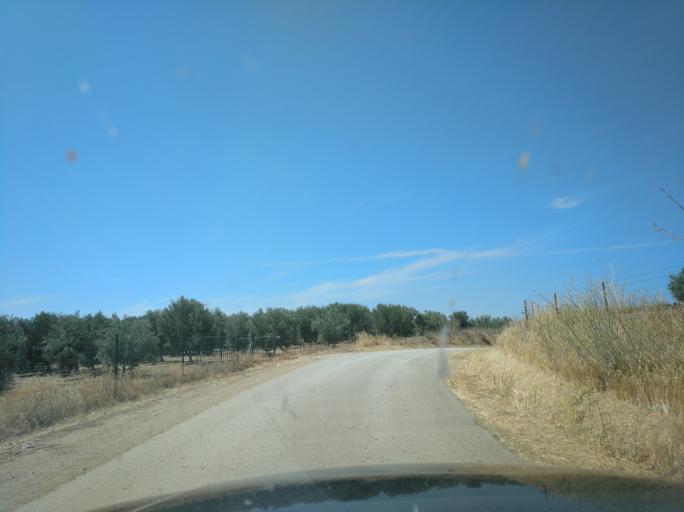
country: PT
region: Portalegre
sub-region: Campo Maior
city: Campo Maior
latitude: 38.9594
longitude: -7.1064
